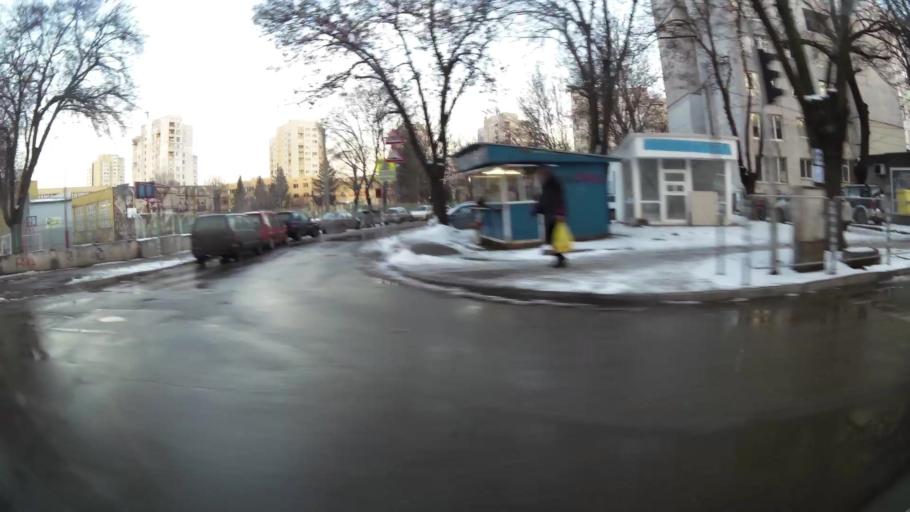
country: BG
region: Sofia-Capital
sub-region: Stolichna Obshtina
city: Sofia
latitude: 42.6848
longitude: 23.3719
